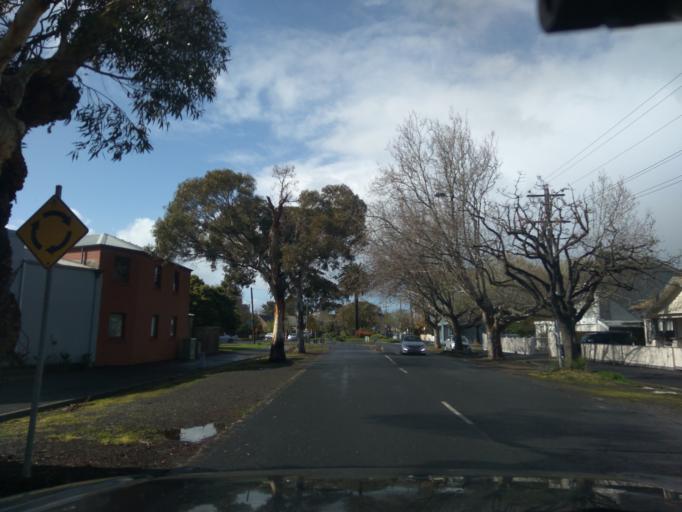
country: AU
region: Victoria
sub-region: Hobsons Bay
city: Williamstown
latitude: -37.8629
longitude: 144.8982
